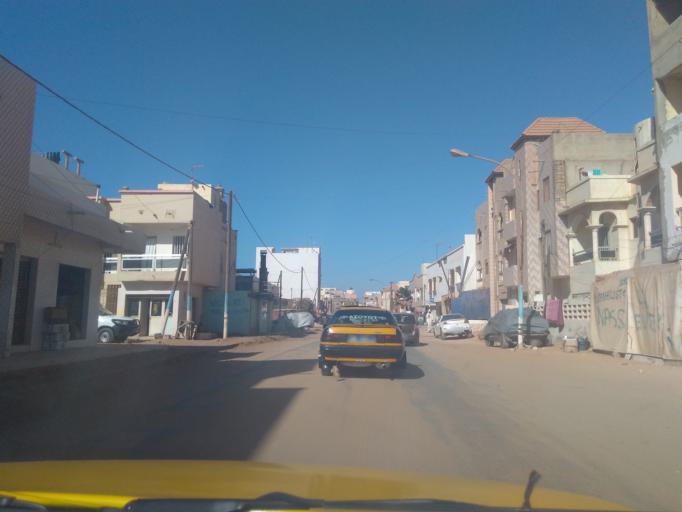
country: SN
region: Dakar
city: Pikine
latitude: 14.7728
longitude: -17.4202
